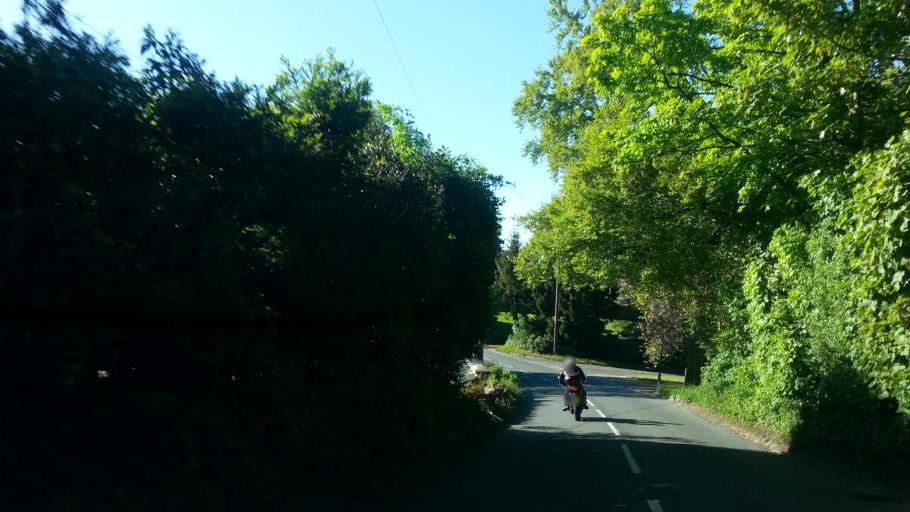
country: GB
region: England
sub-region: Somerset
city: Wincanton
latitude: 51.0112
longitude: -2.4292
